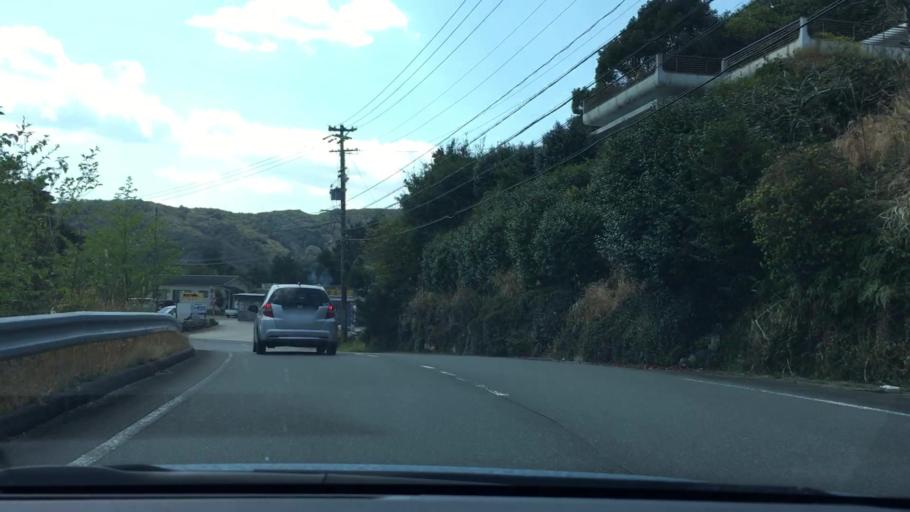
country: JP
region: Mie
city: Toba
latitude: 34.4529
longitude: 136.8745
